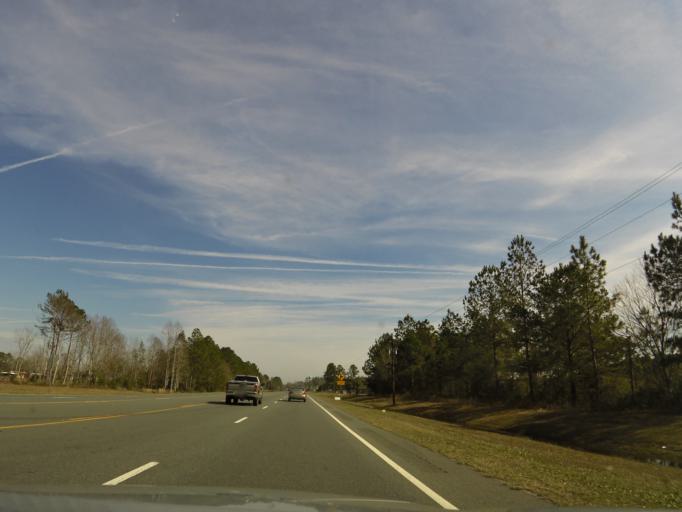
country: US
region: Georgia
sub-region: Pierce County
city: Blackshear
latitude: 31.1795
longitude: -82.1491
